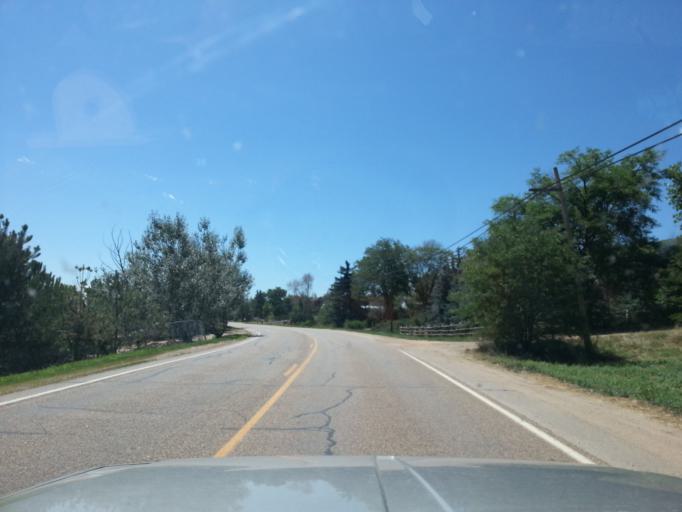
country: US
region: Colorado
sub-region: Larimer County
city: Loveland
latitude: 40.4358
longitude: -105.1971
